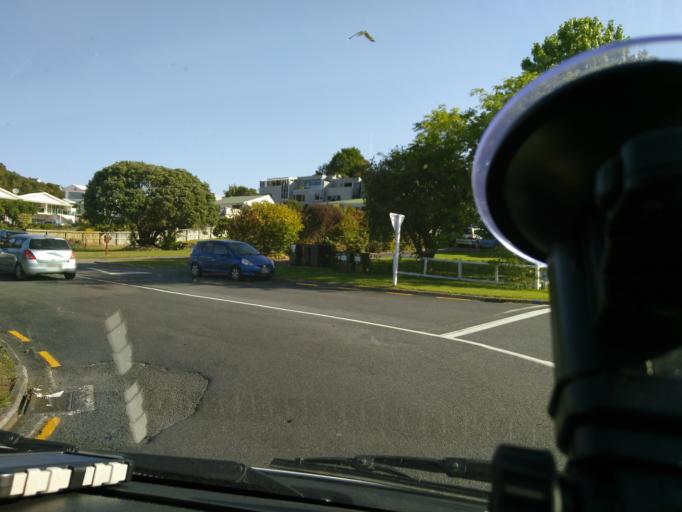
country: NZ
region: Northland
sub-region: Far North District
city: Paihia
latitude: -35.2862
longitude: 174.0943
